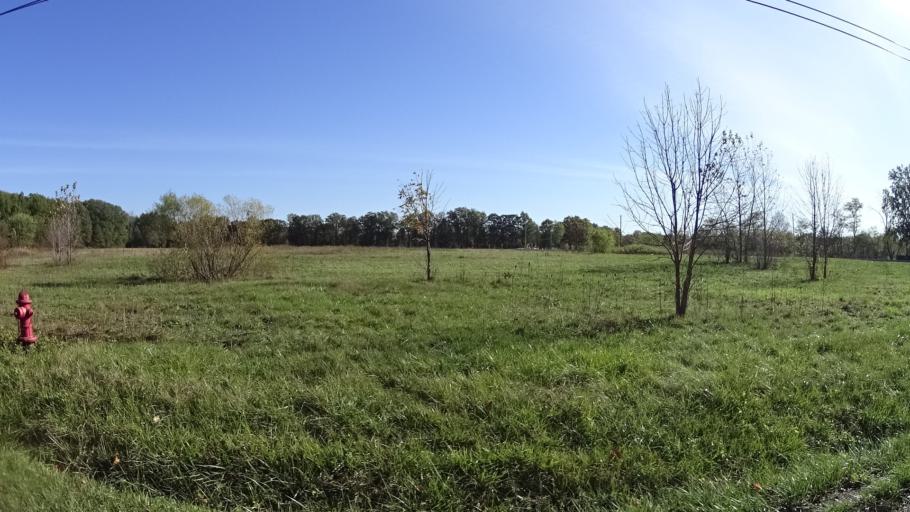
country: US
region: Ohio
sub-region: Lorain County
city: Vermilion-on-the-Lake
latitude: 41.3839
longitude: -82.3177
